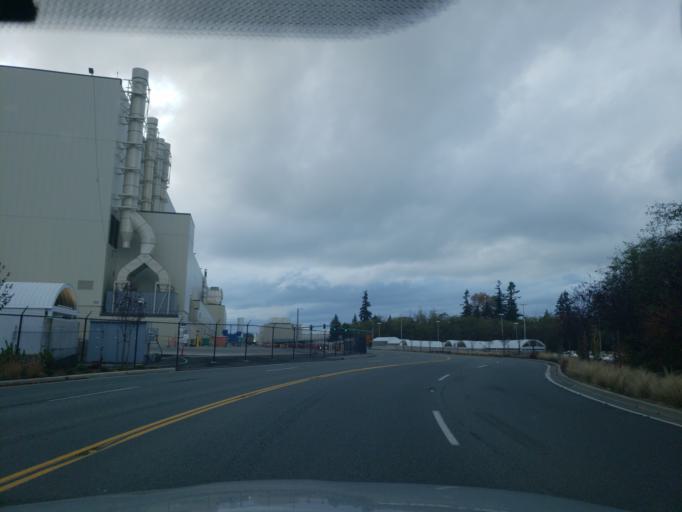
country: US
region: Washington
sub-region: Snohomish County
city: Mukilteo
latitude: 47.9311
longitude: -122.2670
